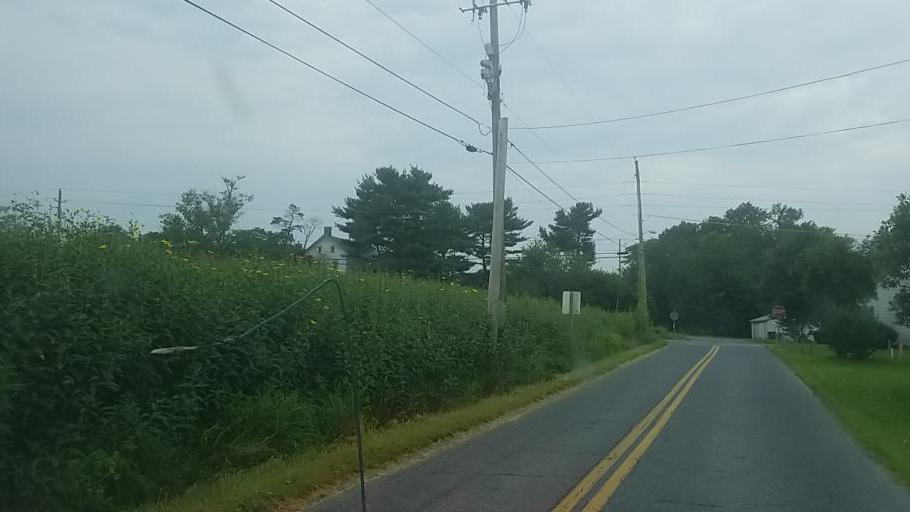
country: US
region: Delaware
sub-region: Sussex County
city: Selbyville
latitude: 38.4411
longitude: -75.1945
